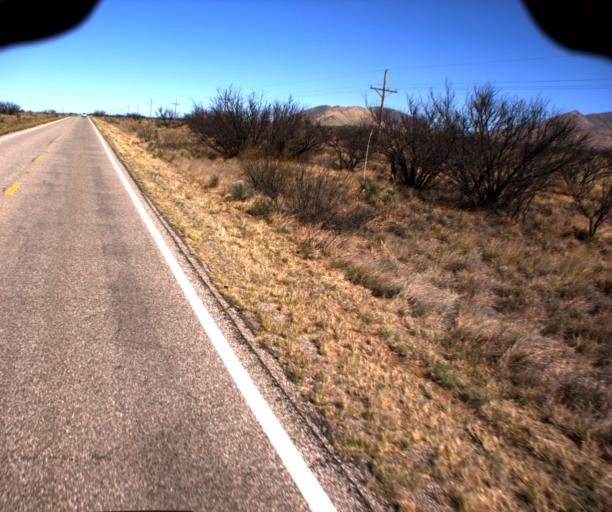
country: US
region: Arizona
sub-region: Cochise County
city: Huachuca City
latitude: 31.7008
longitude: -110.4299
